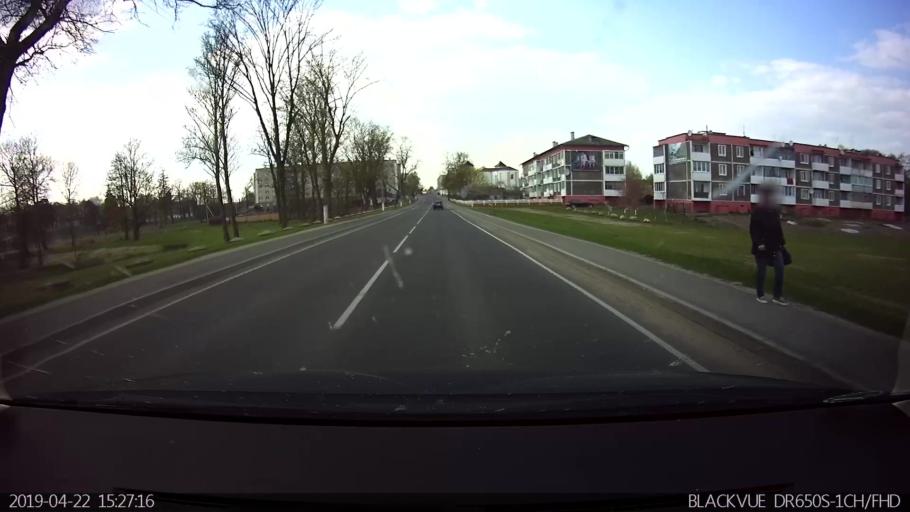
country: BY
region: Brest
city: Vysokaye
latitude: 52.3698
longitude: 23.3733
